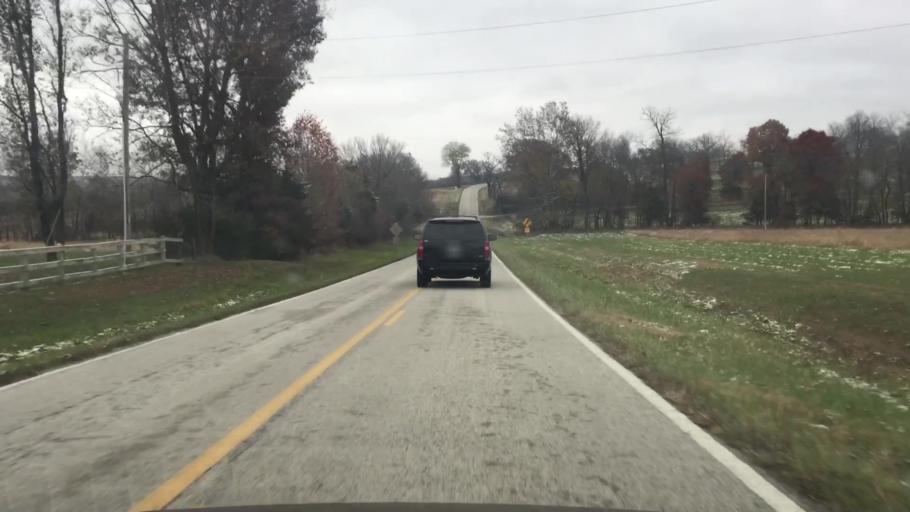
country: US
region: Missouri
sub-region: Saint Clair County
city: Osceola
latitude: 37.9895
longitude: -93.6283
